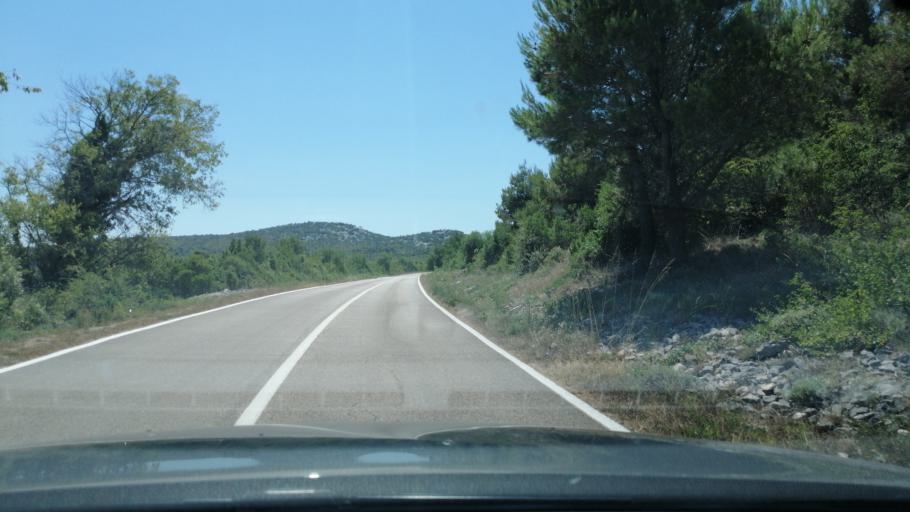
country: HR
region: Sibensko-Kniniska
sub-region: Grad Sibenik
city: Pirovac
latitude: 43.8646
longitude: 15.6889
